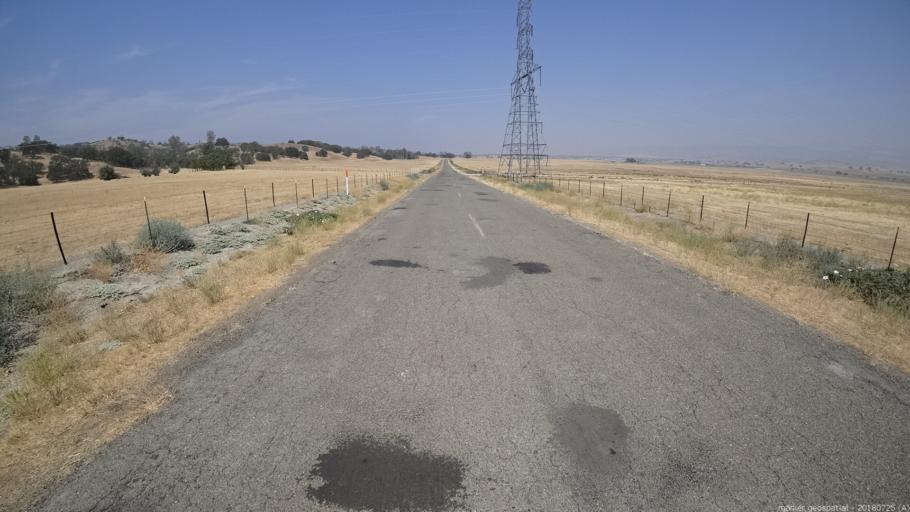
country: US
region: California
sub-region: San Luis Obispo County
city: Shandon
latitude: 35.8178
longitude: -120.3791
